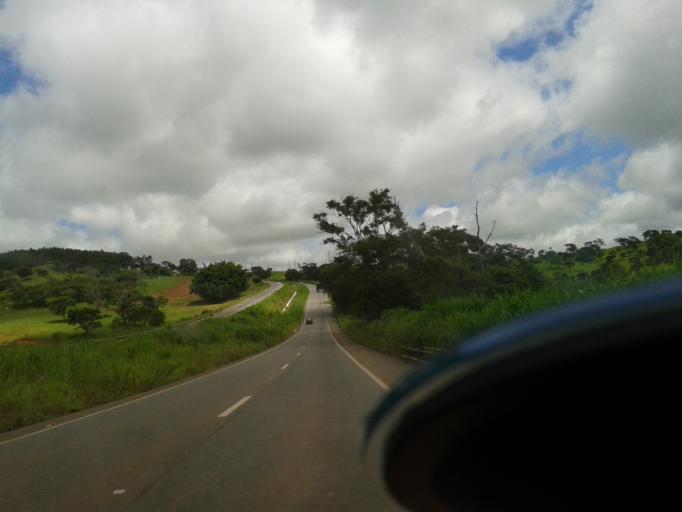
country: BR
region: Goias
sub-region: Inhumas
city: Inhumas
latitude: -16.1665
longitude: -49.6216
